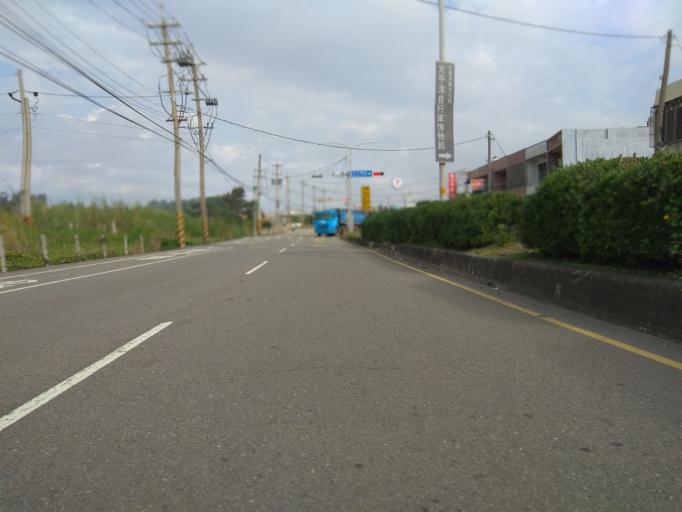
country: TW
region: Taiwan
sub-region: Hsinchu
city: Zhubei
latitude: 24.9857
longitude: 121.0275
